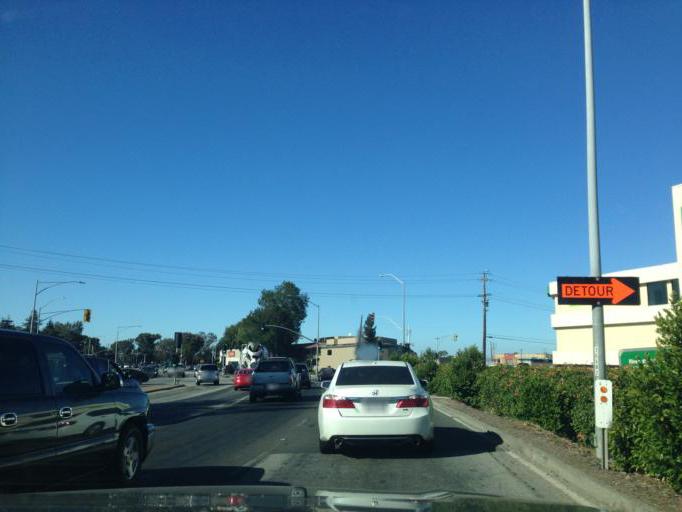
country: US
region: California
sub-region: San Mateo County
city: North Fair Oaks
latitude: 37.4847
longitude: -122.2150
